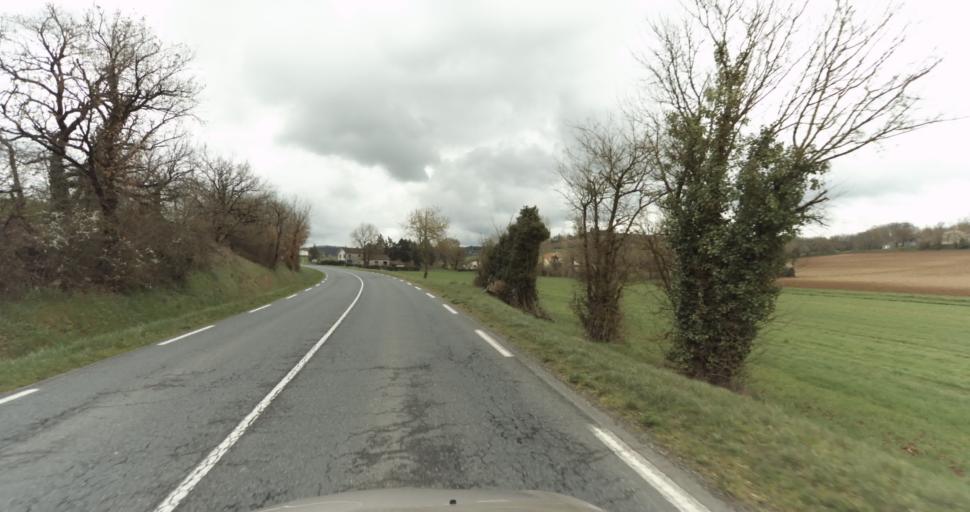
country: FR
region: Midi-Pyrenees
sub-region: Departement du Tarn
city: Puygouzon
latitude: 43.8848
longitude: 2.1676
